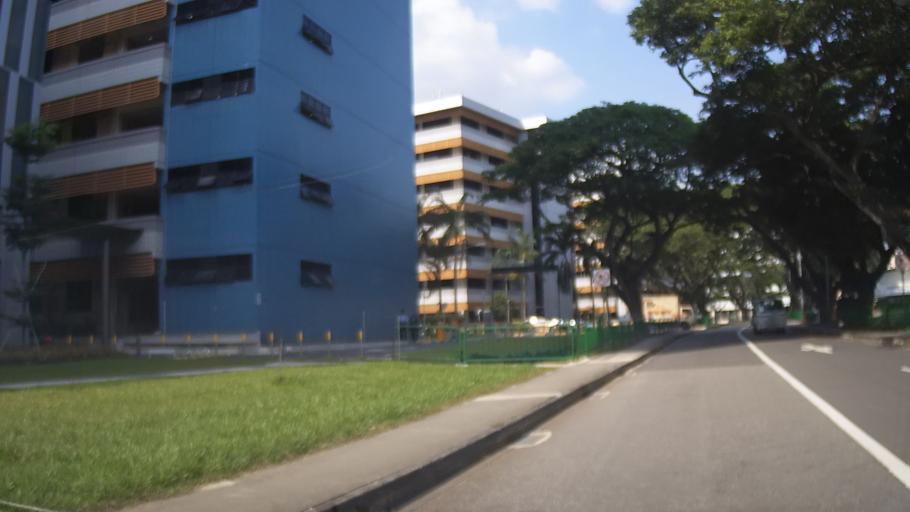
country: SG
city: Singapore
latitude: 1.3141
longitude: 103.8664
